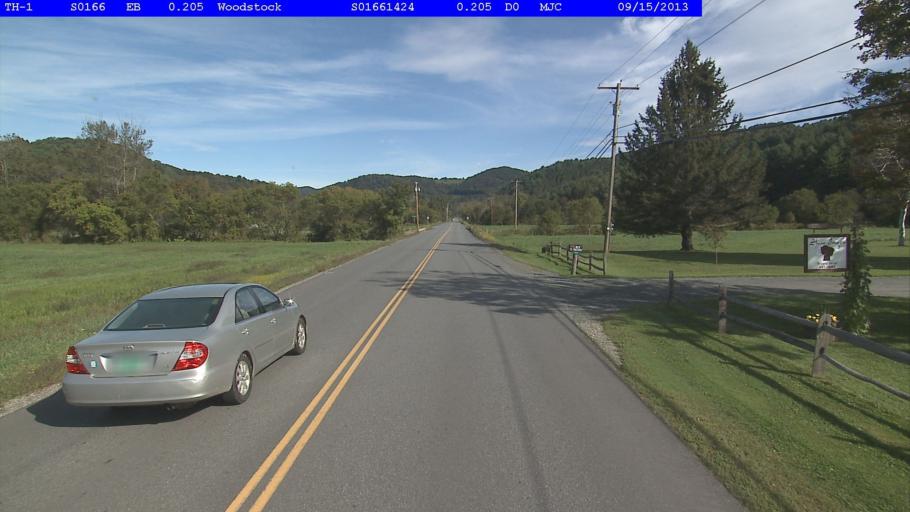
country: US
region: Vermont
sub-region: Windsor County
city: Woodstock
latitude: 43.6412
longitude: -72.5254
